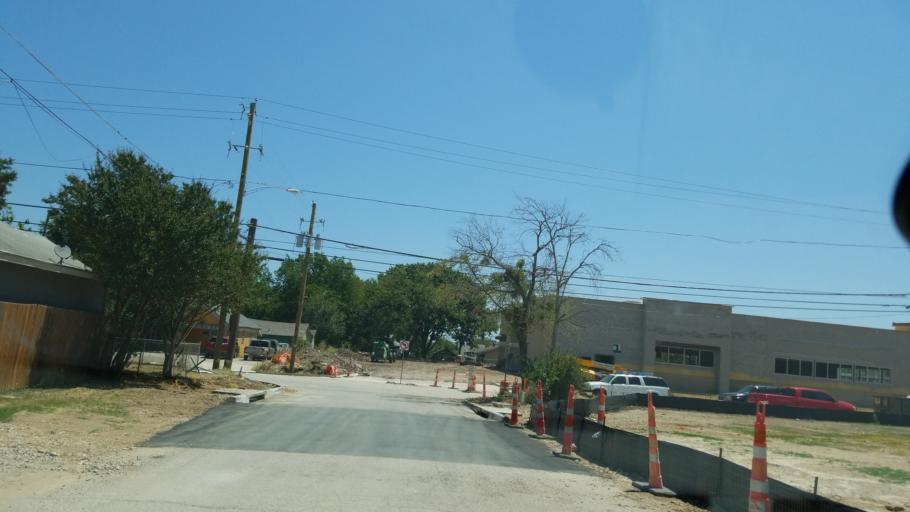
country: US
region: Texas
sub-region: Dallas County
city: Cockrell Hill
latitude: 32.7386
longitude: -96.8919
